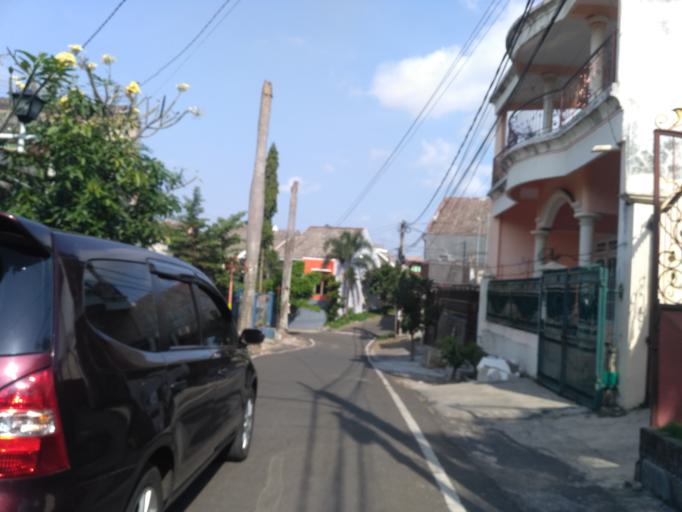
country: ID
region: East Java
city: Malang
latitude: -7.9354
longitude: 112.6082
